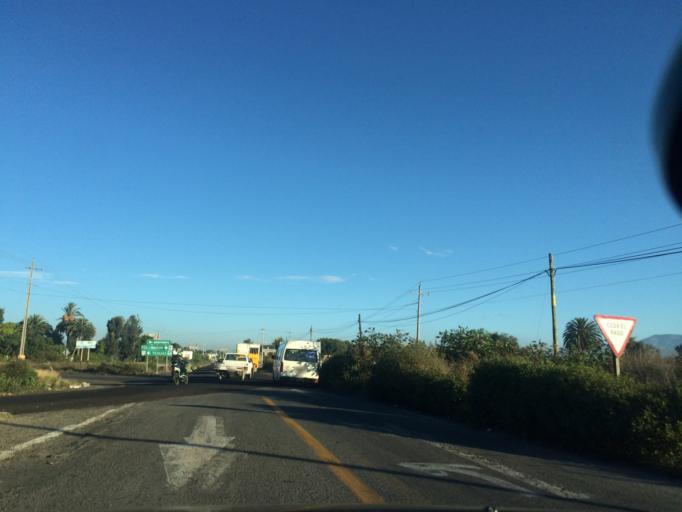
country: MX
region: Puebla
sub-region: Santiago Miahuatlan
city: San Jose Monte Chiquito
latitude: 18.4879
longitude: -97.4575
